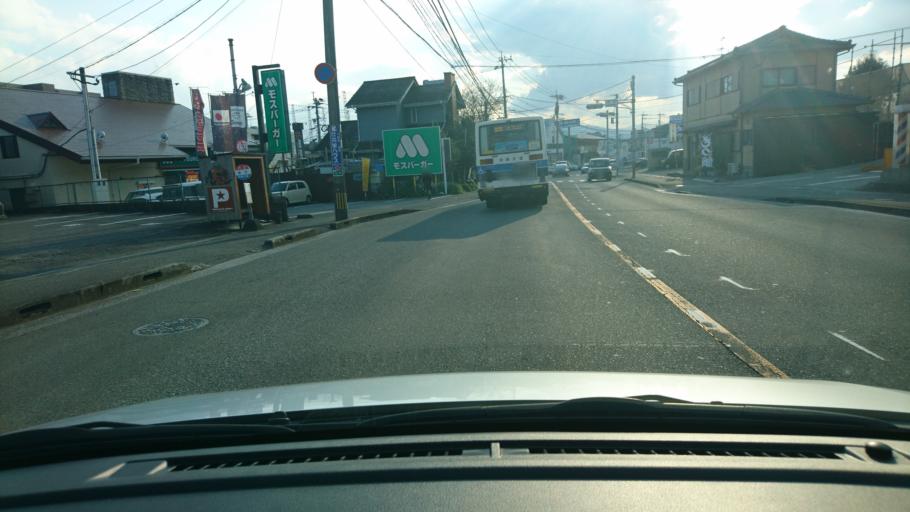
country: JP
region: Miyazaki
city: Miyazaki-shi
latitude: 31.8769
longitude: 131.4054
